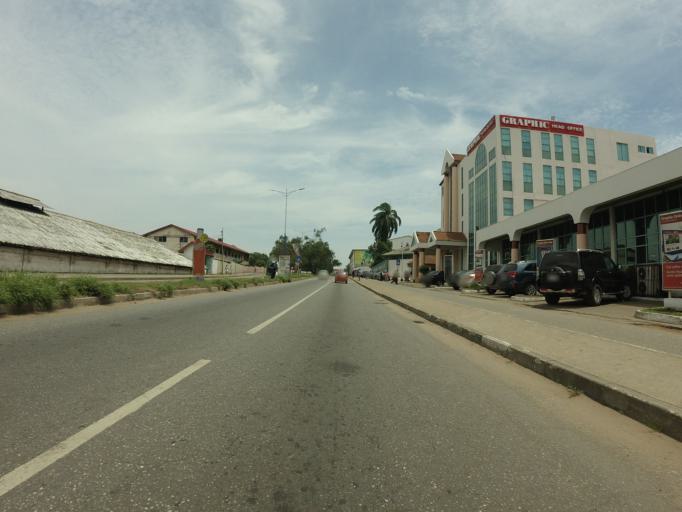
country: GH
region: Greater Accra
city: Accra
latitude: 5.5550
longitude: -0.2174
